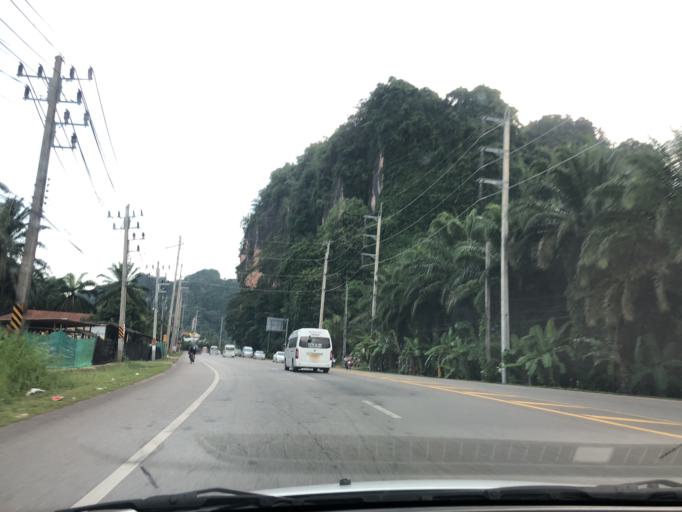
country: TH
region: Krabi
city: Krabi
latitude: 8.0872
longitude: 98.8801
